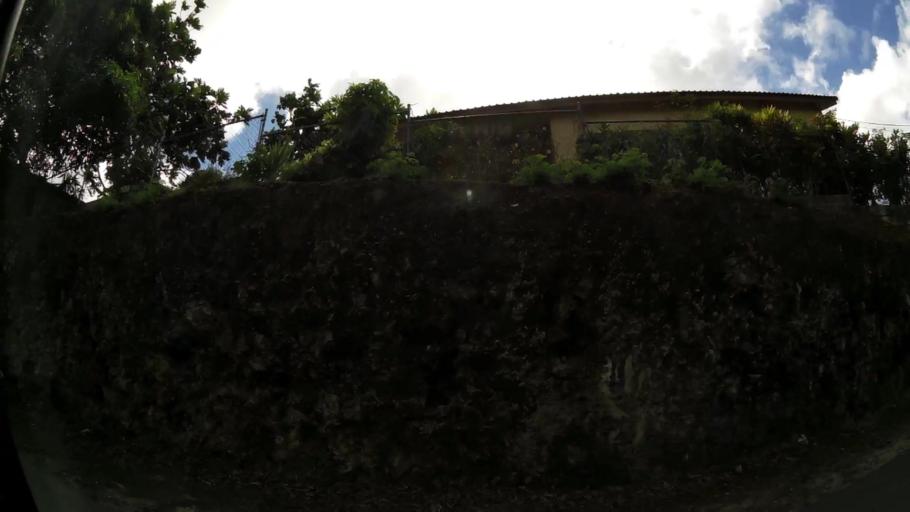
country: BB
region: Saint James
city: Holetown
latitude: 13.2047
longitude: -59.6068
